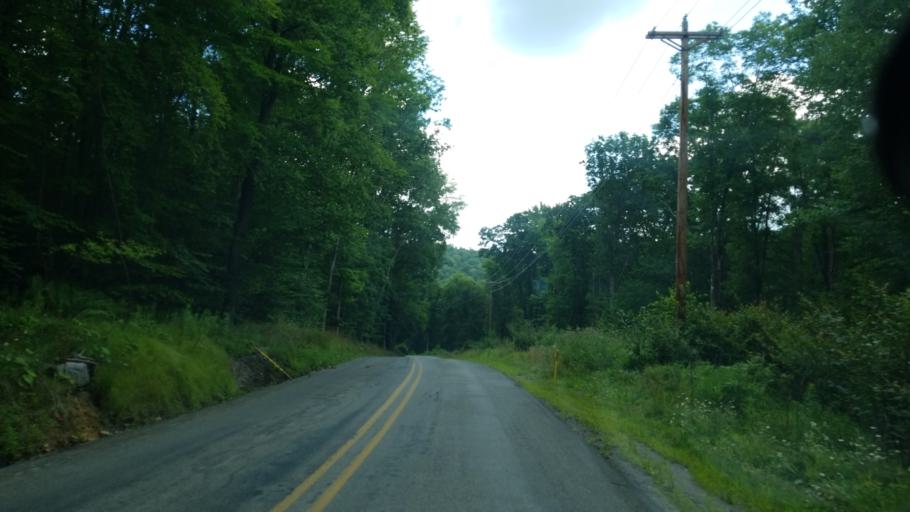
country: US
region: Pennsylvania
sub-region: Jefferson County
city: Brookville
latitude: 41.2273
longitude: -79.0546
